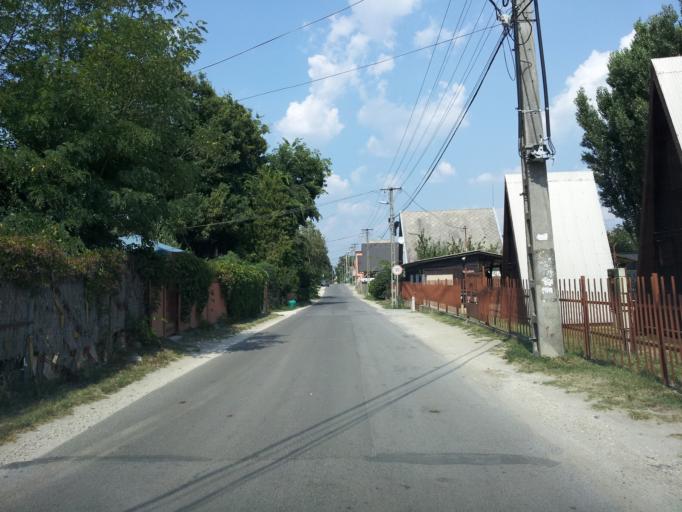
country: HU
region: Pest
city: Szigetszentmiklos
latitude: 47.3217
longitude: 19.0396
